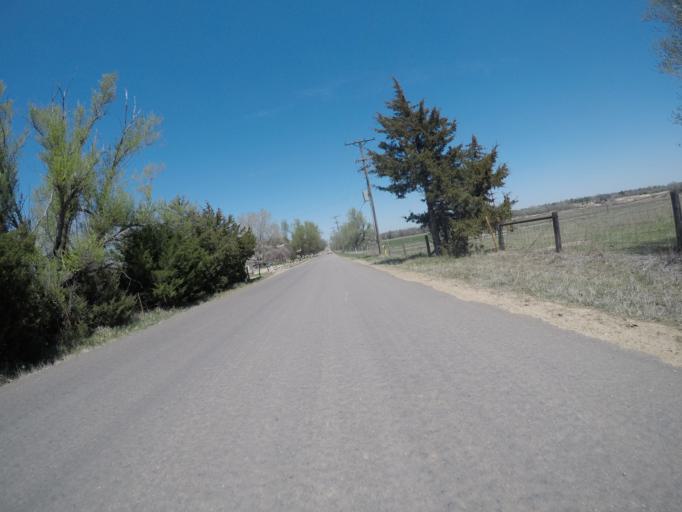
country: US
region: Kansas
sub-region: Pratt County
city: Pratt
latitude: 37.6331
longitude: -98.7670
